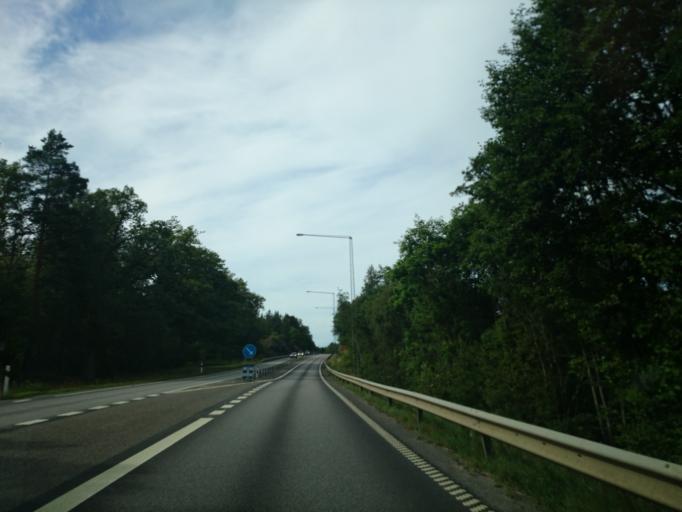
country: SE
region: Kalmar
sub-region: Oskarshamns Kommun
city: Oskarshamn
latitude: 57.3380
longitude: 16.4841
